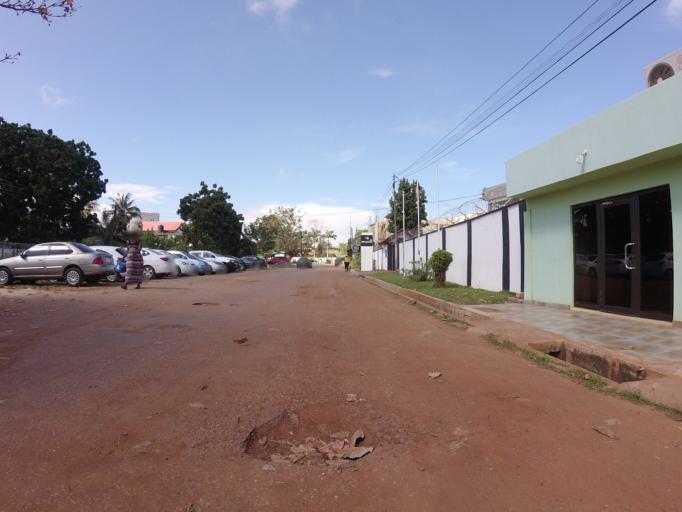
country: GH
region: Greater Accra
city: Accra
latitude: 5.5715
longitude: -0.1716
